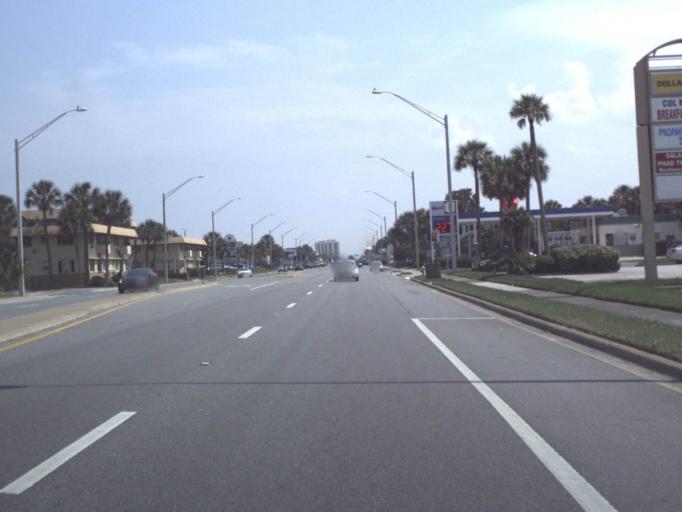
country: US
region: Florida
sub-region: Duval County
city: Neptune Beach
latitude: 30.3047
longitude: -81.3952
